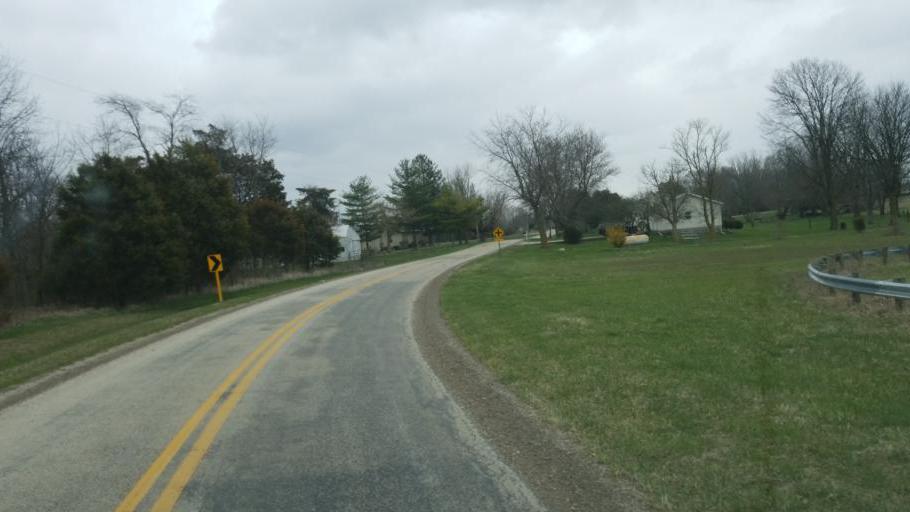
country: US
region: Ohio
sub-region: Marion County
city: Prospect
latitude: 40.4053
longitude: -83.2252
